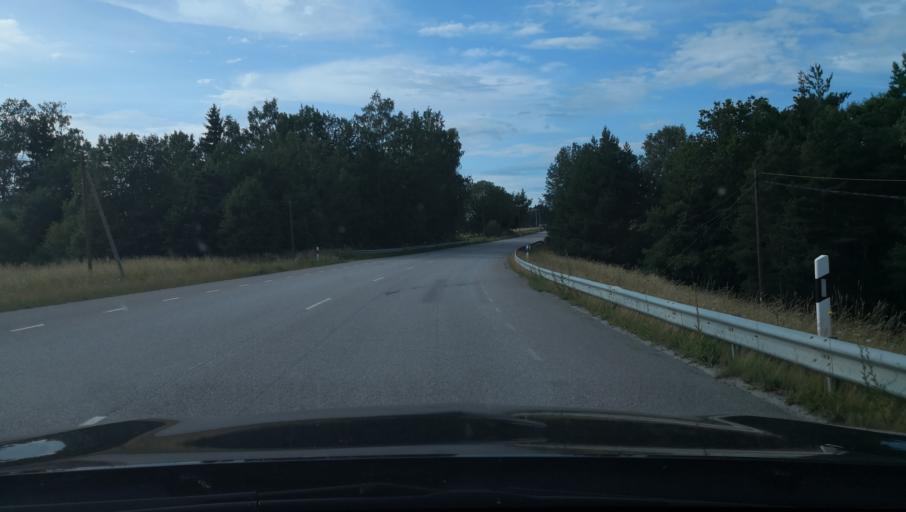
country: SE
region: Uppsala
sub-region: Habo Kommun
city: Balsta
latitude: 59.6077
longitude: 17.5024
